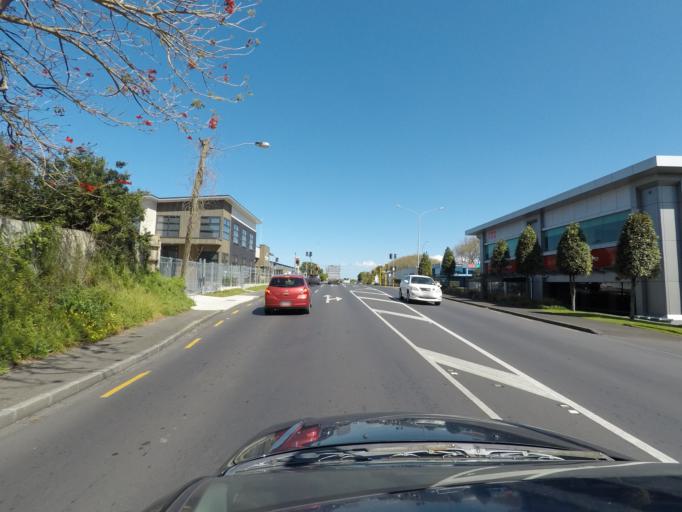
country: NZ
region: Auckland
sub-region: Auckland
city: Tamaki
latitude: -36.9276
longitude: 174.8432
